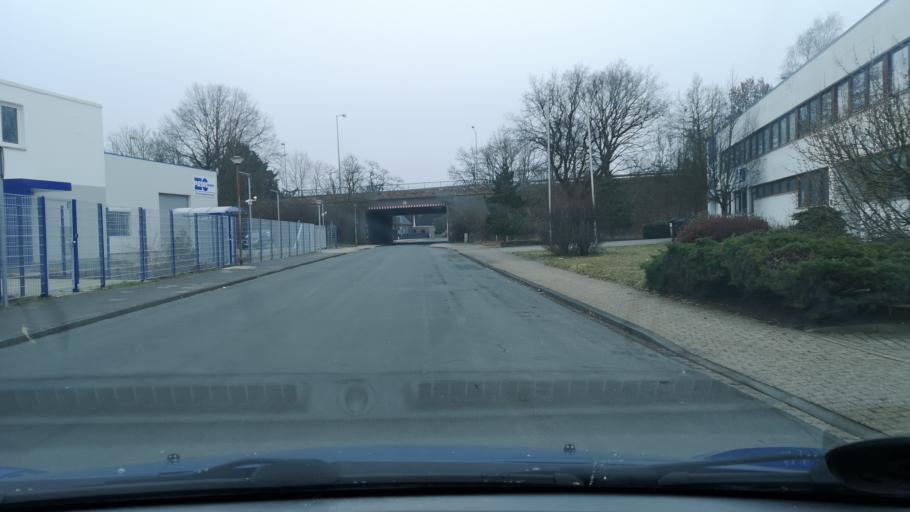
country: DE
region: Lower Saxony
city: Celle
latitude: 52.6078
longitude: 10.0598
